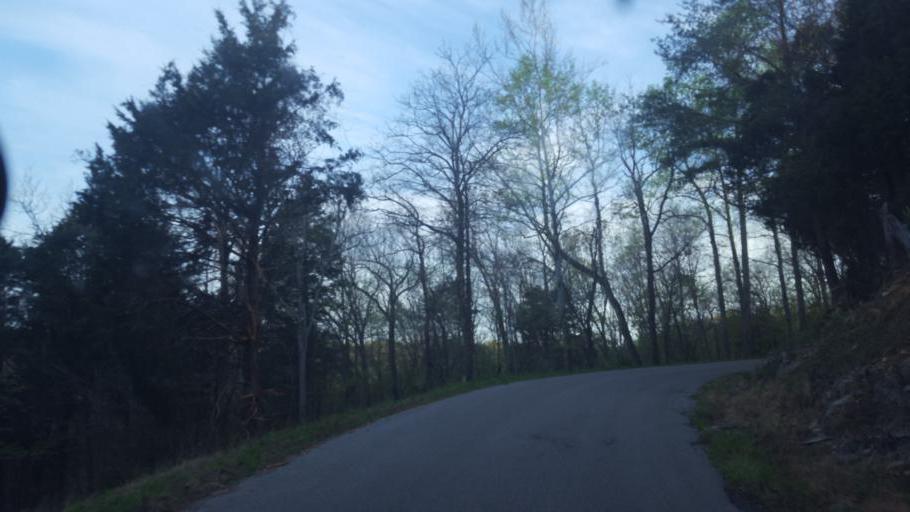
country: US
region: Kentucky
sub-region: Barren County
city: Cave City
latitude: 37.2074
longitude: -86.0157
